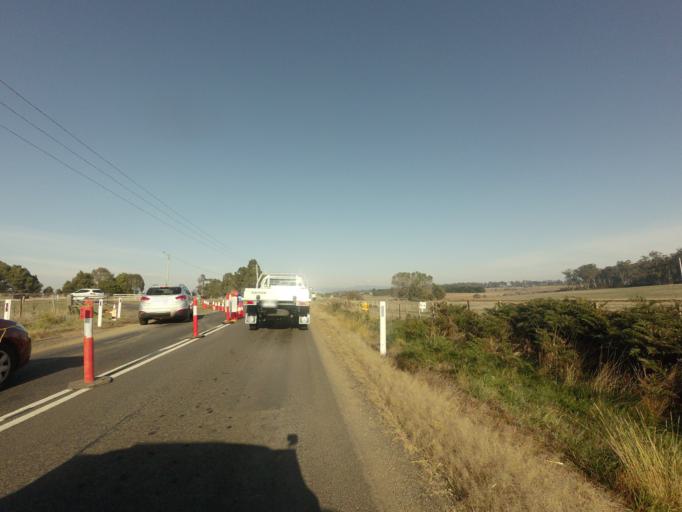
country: AU
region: Tasmania
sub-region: Northern Midlands
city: Longford
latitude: -41.5610
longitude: 146.9827
